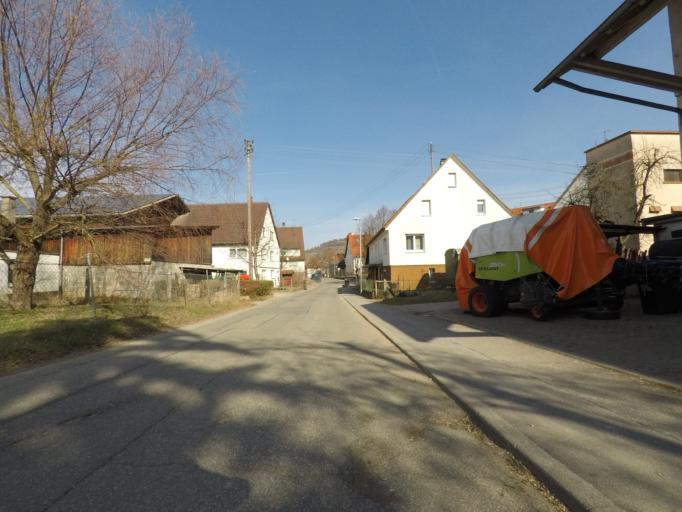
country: DE
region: Baden-Wuerttemberg
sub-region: Tuebingen Region
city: Metzingen
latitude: 48.5264
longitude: 9.3049
